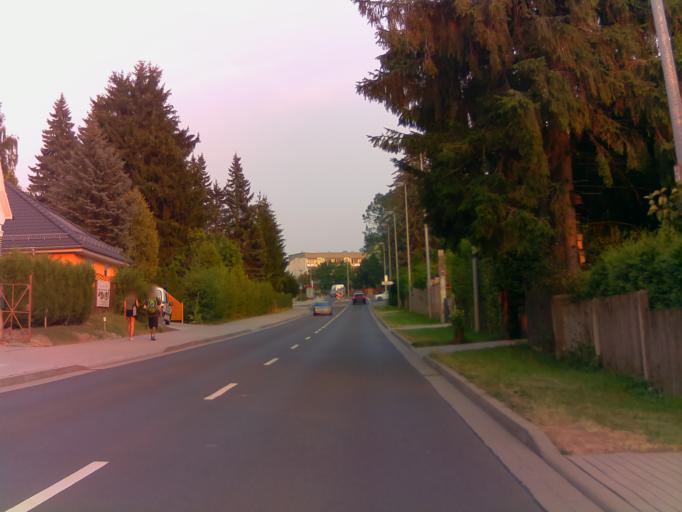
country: DE
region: Thuringia
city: Bad Berka
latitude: 50.8961
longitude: 11.2913
